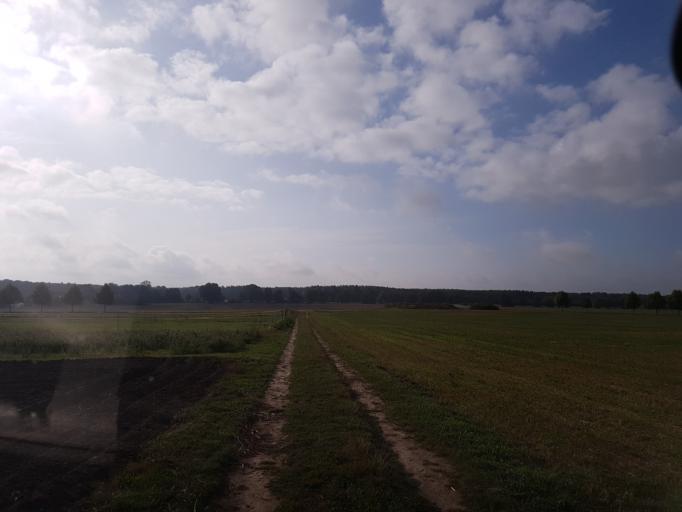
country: DE
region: Brandenburg
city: Finsterwalde
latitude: 51.6257
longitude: 13.7660
